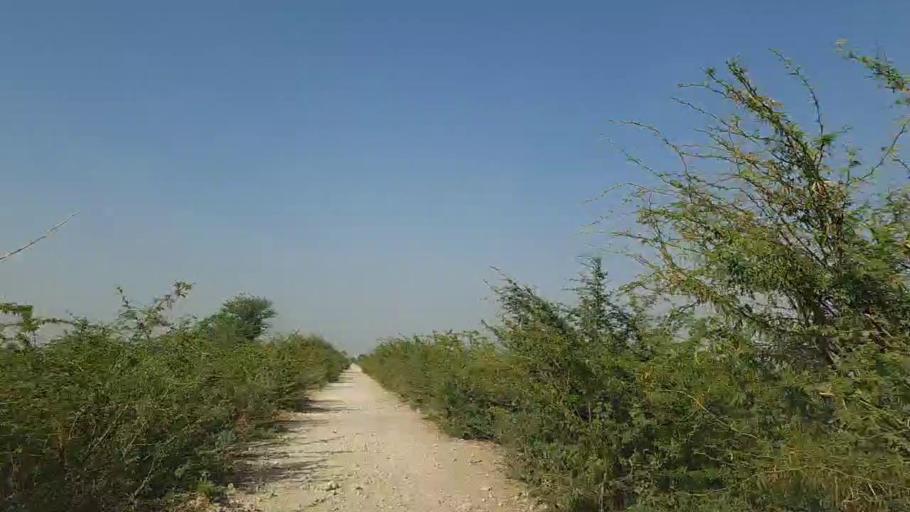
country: PK
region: Sindh
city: Naukot
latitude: 24.9188
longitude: 69.4878
